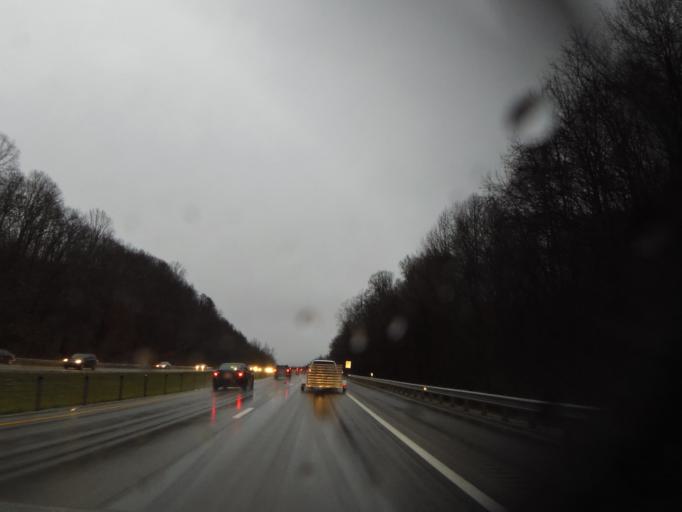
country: US
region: Kentucky
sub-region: Rockcastle County
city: Mount Vernon
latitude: 37.3322
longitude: -84.3045
